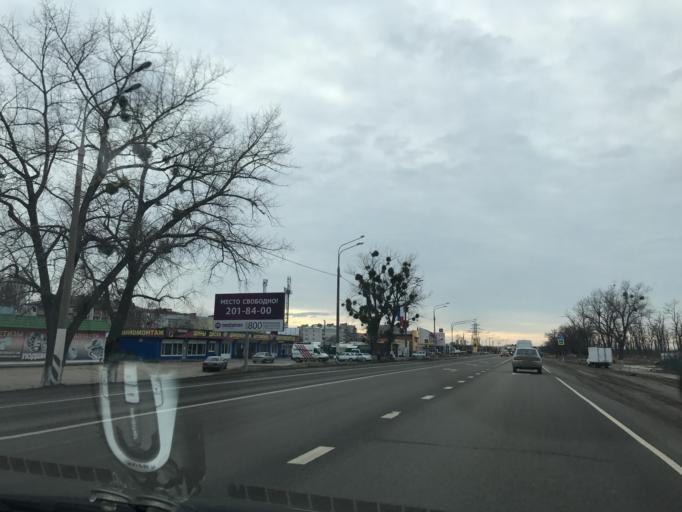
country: RU
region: Krasnodarskiy
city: Kropotkin
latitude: 45.4179
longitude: 40.5434
